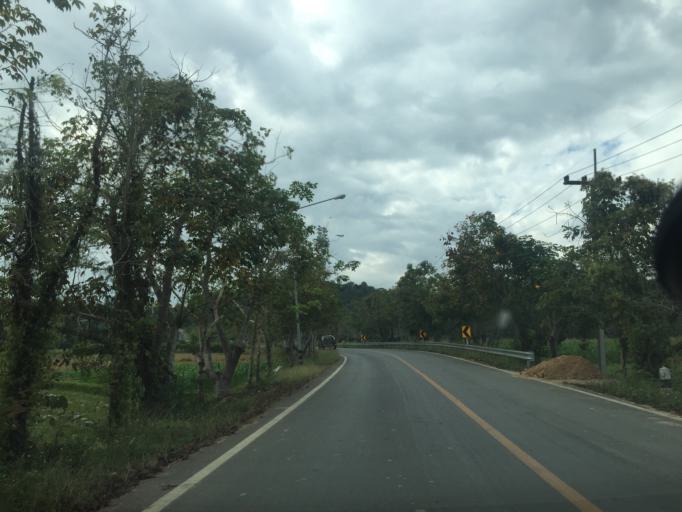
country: TH
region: Lampang
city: Mueang Pan
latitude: 18.7737
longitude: 99.5246
